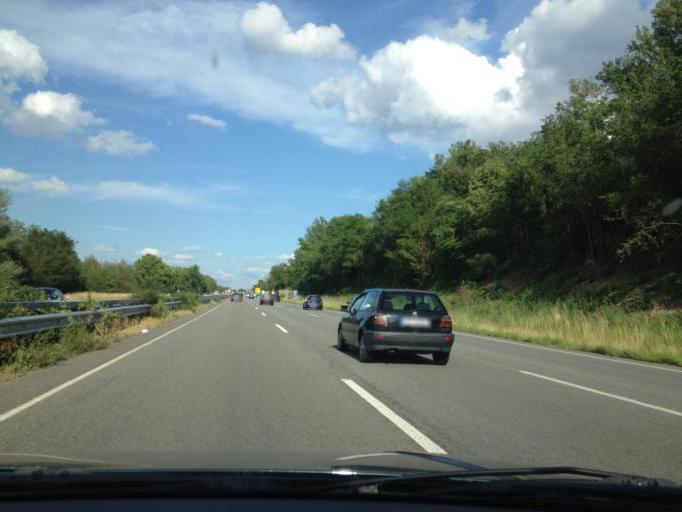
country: DE
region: Rheinland-Pfalz
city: Gartenstadt
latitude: 49.4774
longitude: 8.3984
